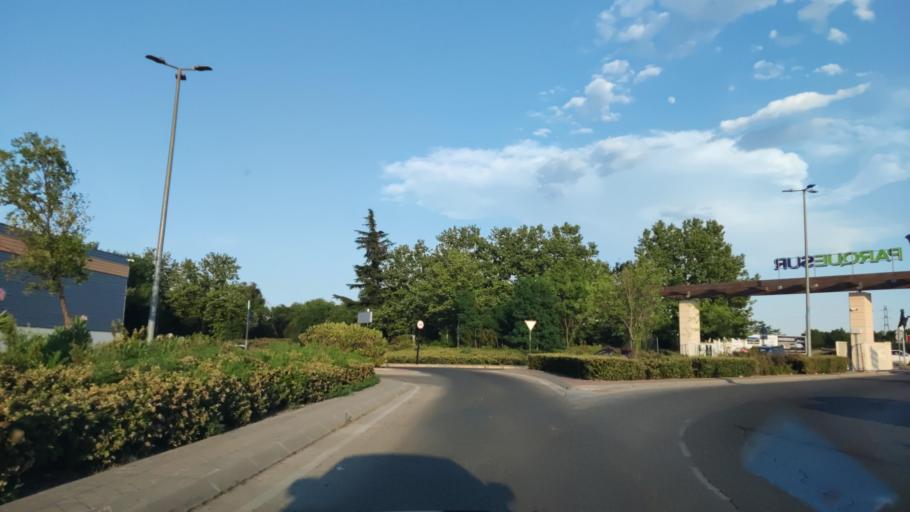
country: ES
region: Madrid
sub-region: Provincia de Madrid
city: Leganes
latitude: 40.3377
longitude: -3.7342
